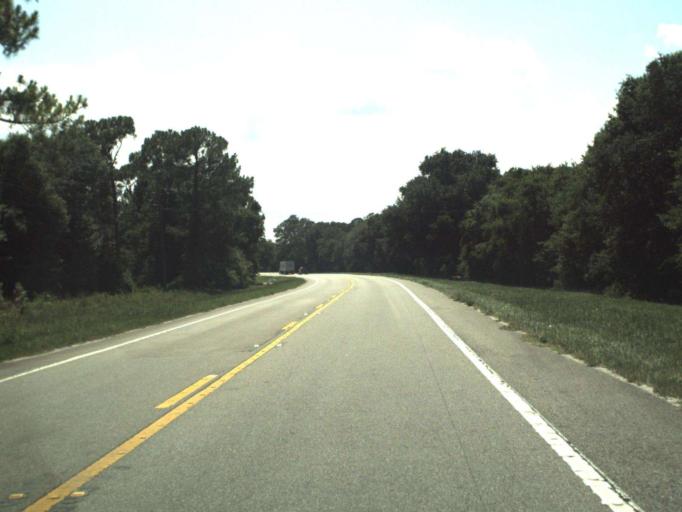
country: US
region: Florida
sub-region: Lake County
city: Mascotte
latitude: 28.5807
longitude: -81.9704
